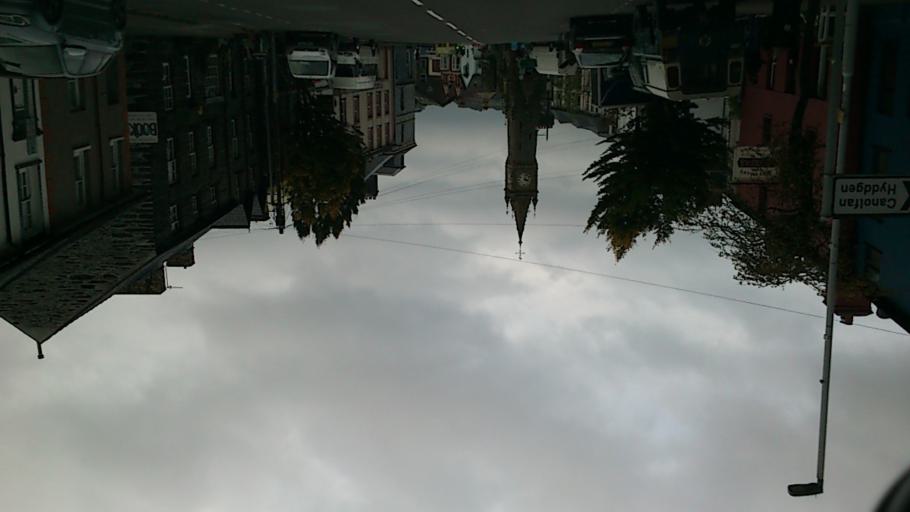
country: GB
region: Wales
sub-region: Sir Powys
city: Machynlleth
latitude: 52.5896
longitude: -3.8531
